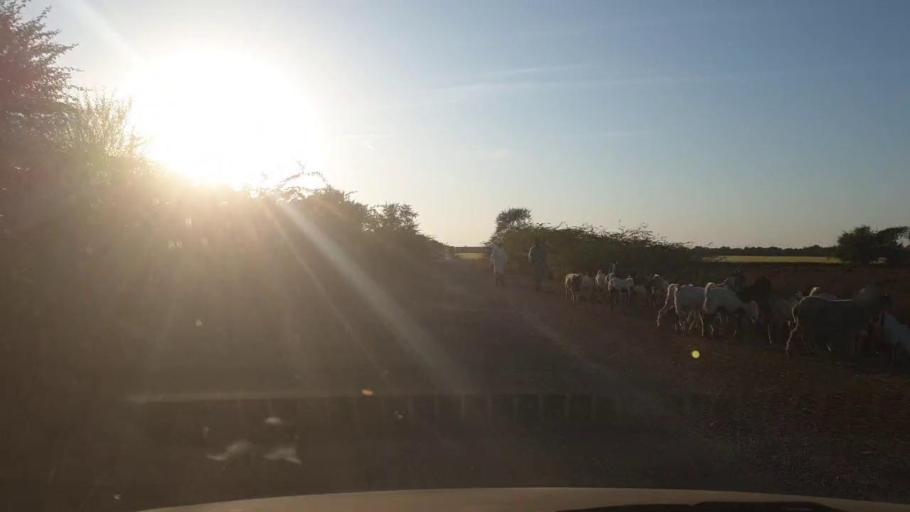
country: PK
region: Sindh
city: Dhoro Naro
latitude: 25.3634
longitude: 69.5663
